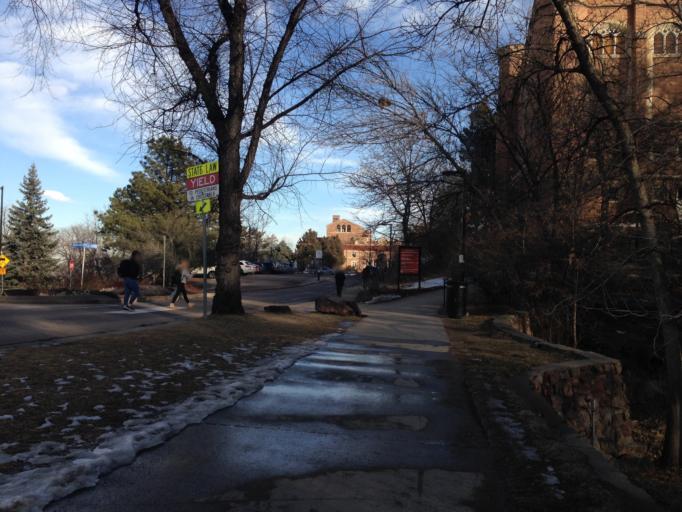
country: US
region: Colorado
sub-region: Boulder County
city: Boulder
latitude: 40.0104
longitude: -105.2736
